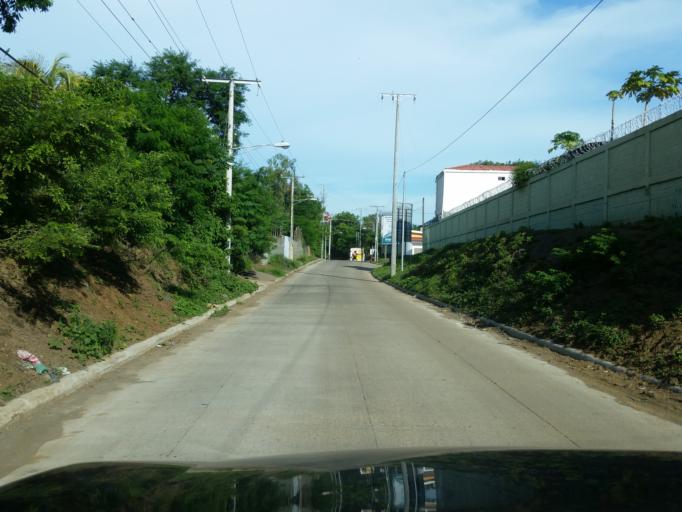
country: NI
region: Managua
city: Managua
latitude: 12.0942
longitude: -86.2033
